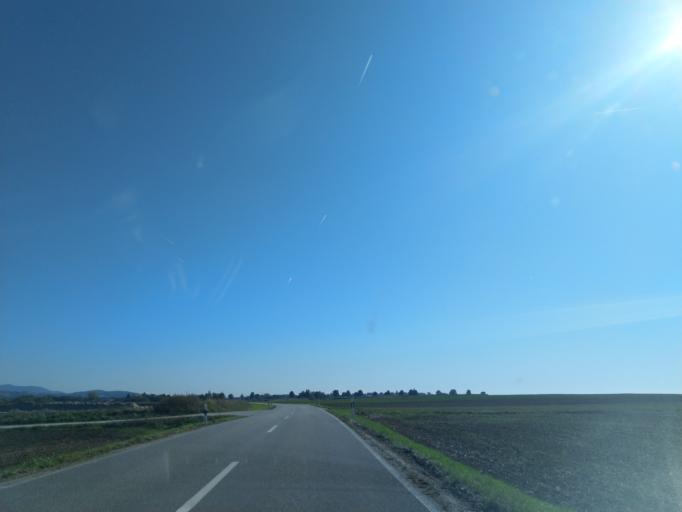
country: DE
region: Bavaria
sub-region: Lower Bavaria
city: Offenberg
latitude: 48.8231
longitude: 12.8679
